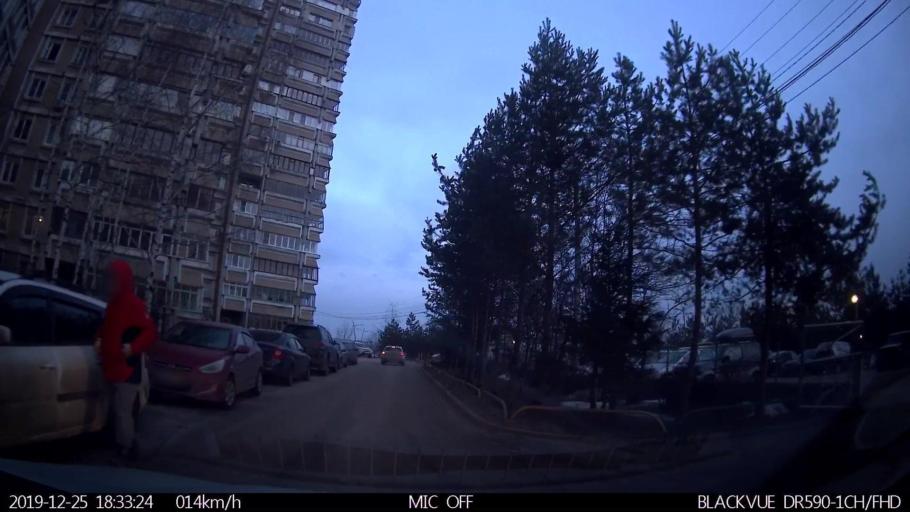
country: RU
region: Nizjnij Novgorod
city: Nizhniy Novgorod
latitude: 56.3447
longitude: 43.9421
